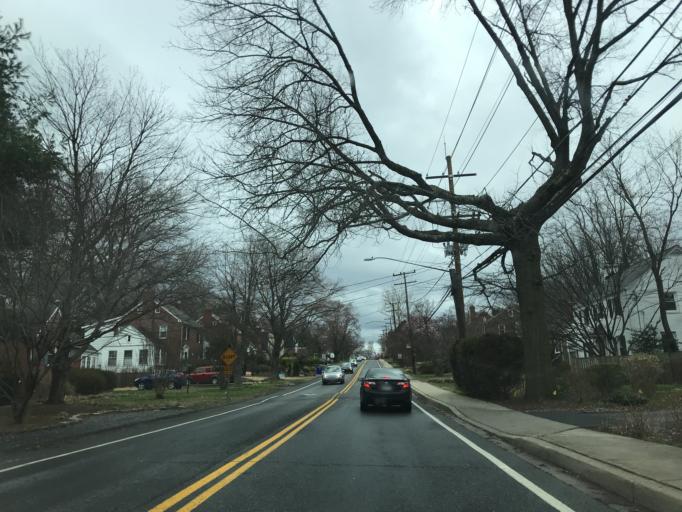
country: US
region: Maryland
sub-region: Montgomery County
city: Four Corners
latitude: 39.0067
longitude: -77.0076
